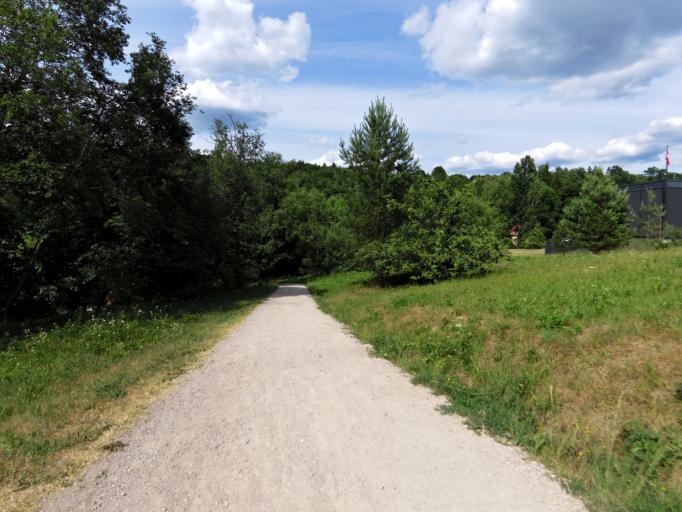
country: LT
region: Vilnius County
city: Rasos
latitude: 54.6888
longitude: 25.3543
